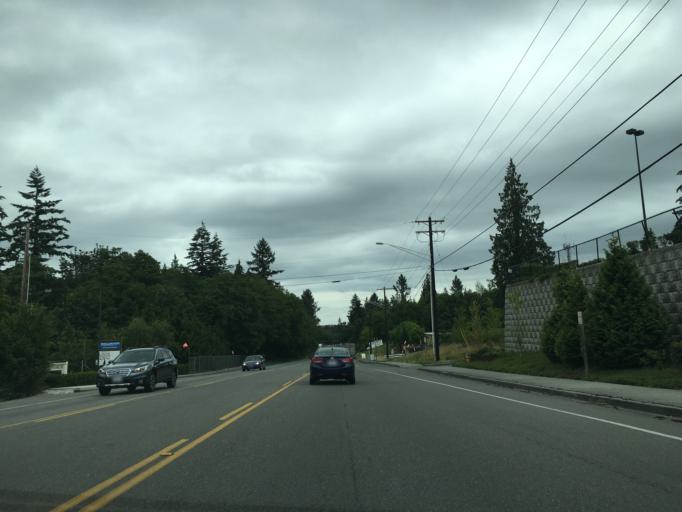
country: US
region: Washington
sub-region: Snohomish County
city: Alderwood Manor
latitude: 47.8470
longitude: -122.2712
